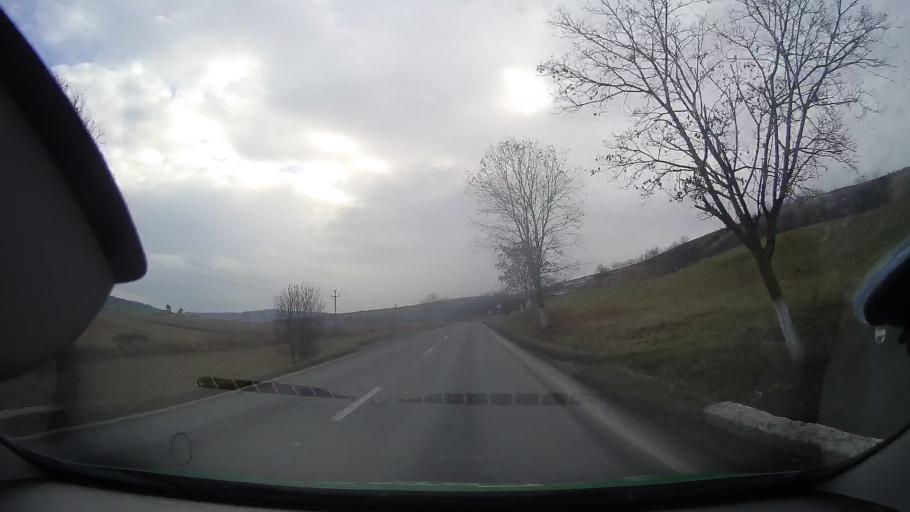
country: RO
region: Mures
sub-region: Comuna Cucerdea
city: Cucerdea
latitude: 46.3859
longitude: 24.2550
